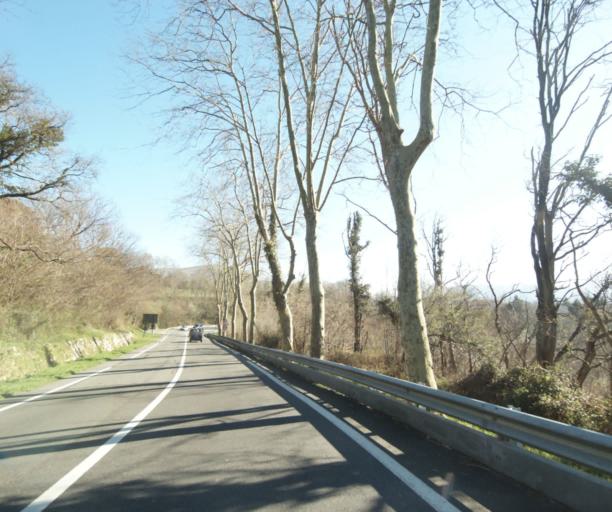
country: FR
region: Aquitaine
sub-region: Departement des Pyrenees-Atlantiques
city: Hendaye
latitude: 43.3516
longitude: -1.7388
